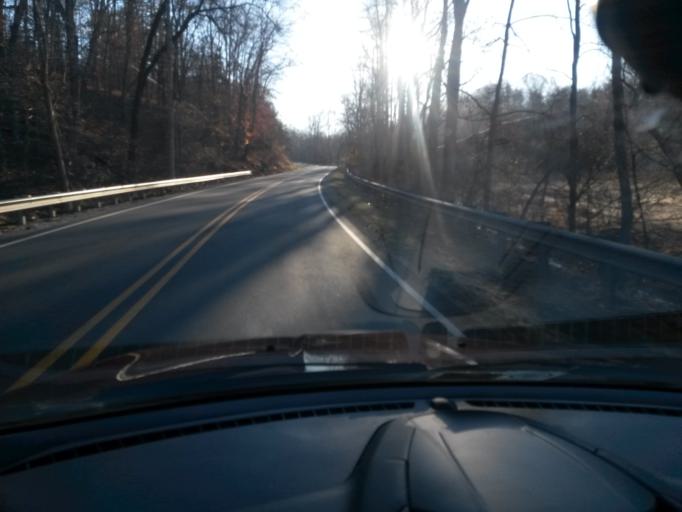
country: US
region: Virginia
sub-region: Amherst County
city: Amherst
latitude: 37.6134
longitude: -79.0862
